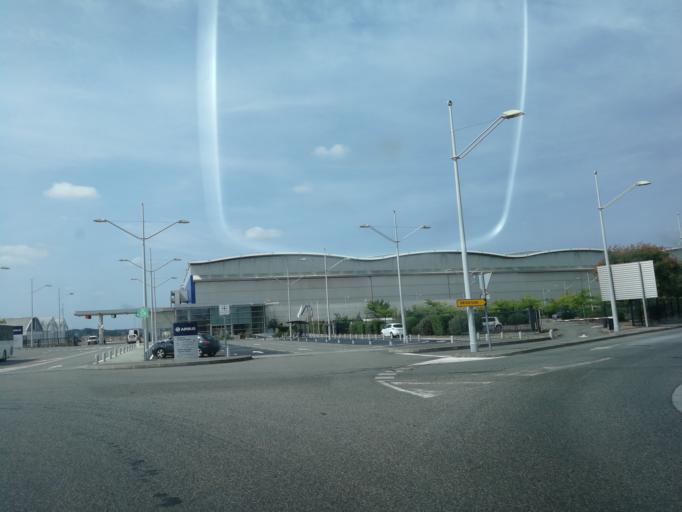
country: FR
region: Midi-Pyrenees
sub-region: Departement de la Haute-Garonne
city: Beauzelle
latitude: 43.6549
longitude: 1.3607
